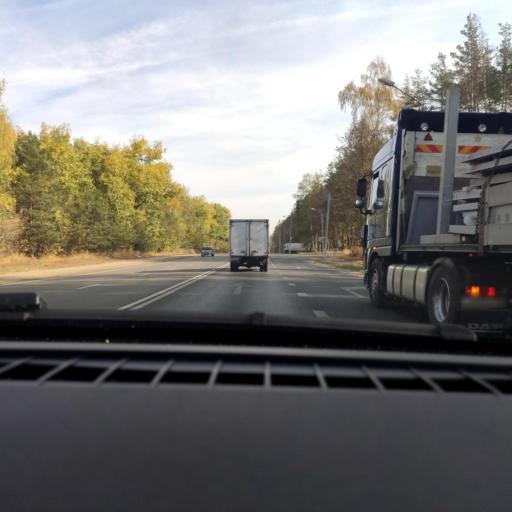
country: RU
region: Voronezj
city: Somovo
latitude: 51.6875
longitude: 39.2915
